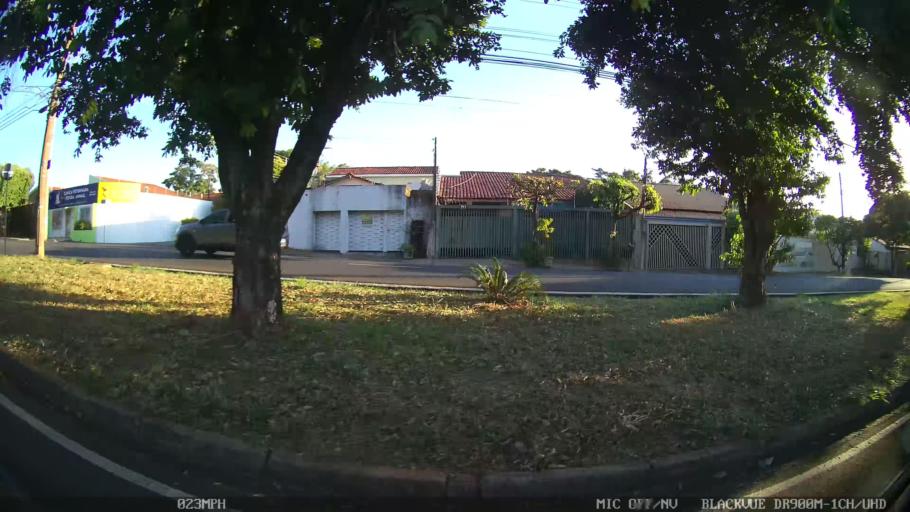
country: BR
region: Sao Paulo
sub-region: Sao Jose Do Rio Preto
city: Sao Jose do Rio Preto
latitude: -20.7798
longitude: -49.3656
